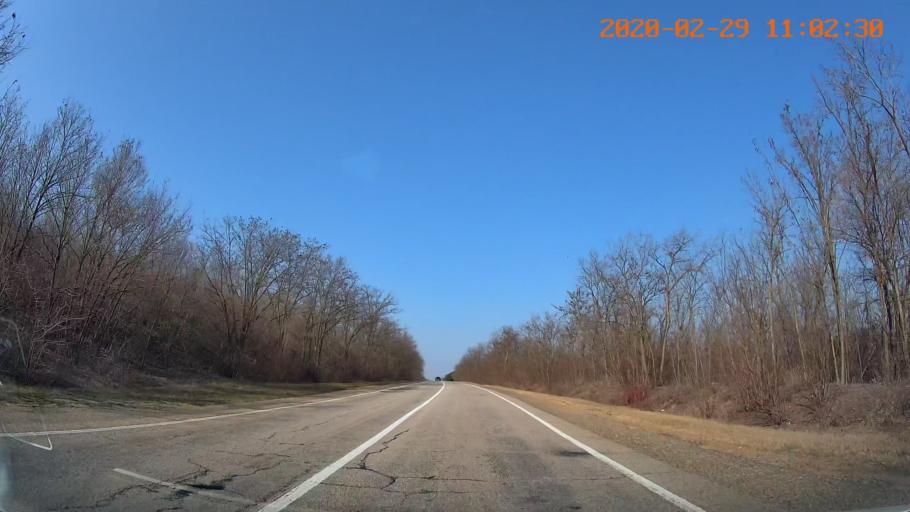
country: MD
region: Telenesti
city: Grigoriopol
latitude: 47.1730
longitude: 29.2367
